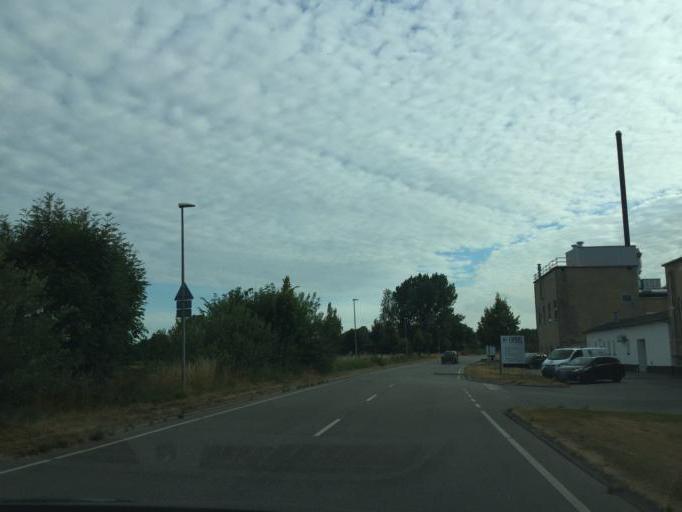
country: DK
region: South Denmark
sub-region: Assens Kommune
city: Assens
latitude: 55.2439
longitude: 9.9649
